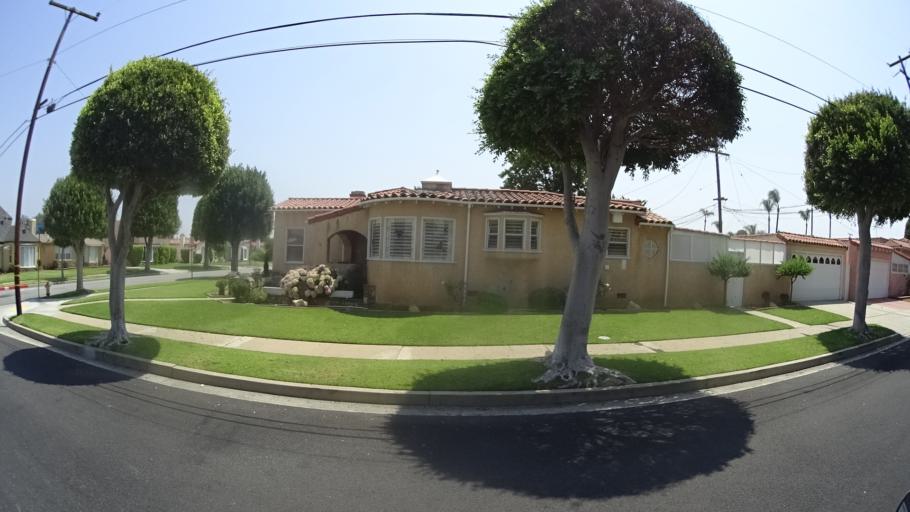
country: US
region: California
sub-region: Los Angeles County
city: Inglewood
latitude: 33.9676
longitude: -118.3347
